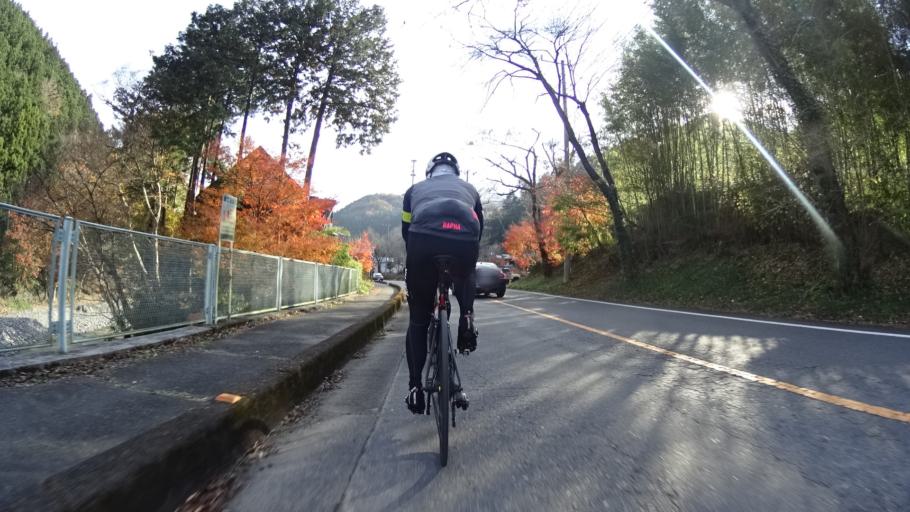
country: JP
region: Tokyo
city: Ome
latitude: 35.8639
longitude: 139.1869
